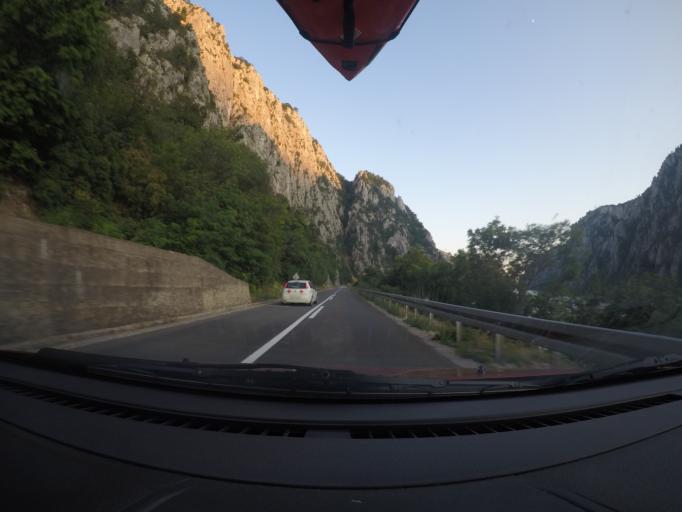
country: RO
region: Mehedinti
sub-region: Comuna Dubova
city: Dubova
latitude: 44.6166
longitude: 22.2747
